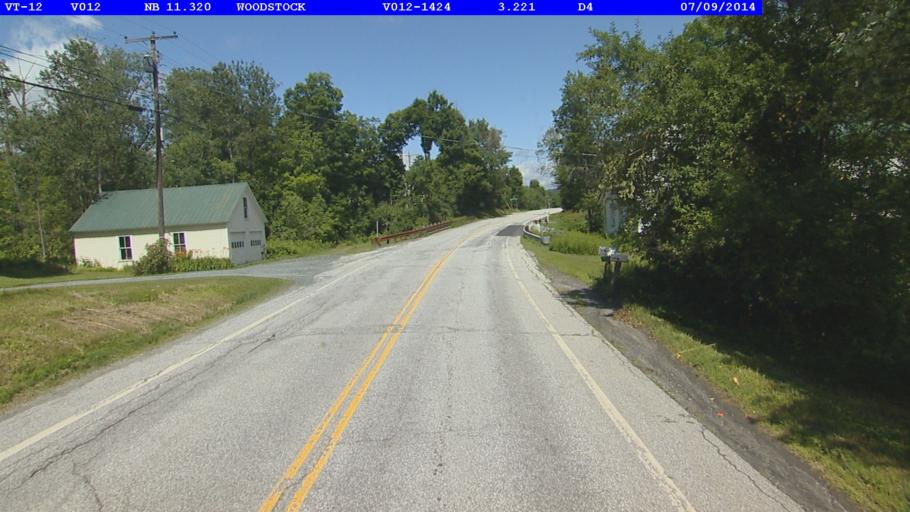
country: US
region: Vermont
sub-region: Windsor County
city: Woodstock
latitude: 43.6482
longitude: -72.5586
